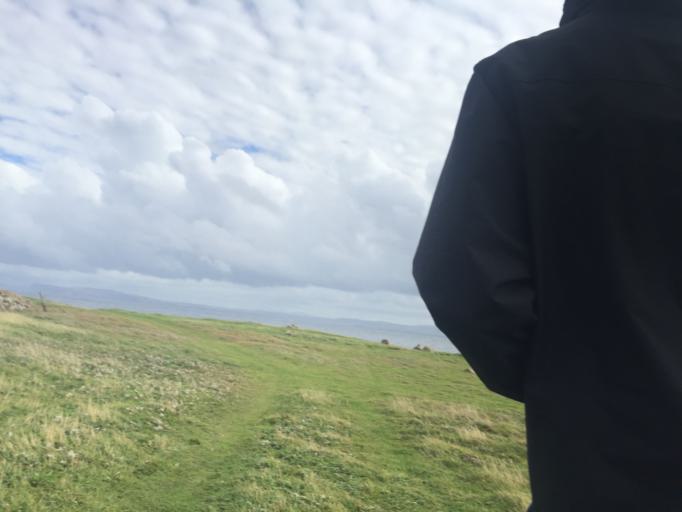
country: IE
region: Ulster
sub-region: County Donegal
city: Derrybeg
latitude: 55.2544
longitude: -8.1981
